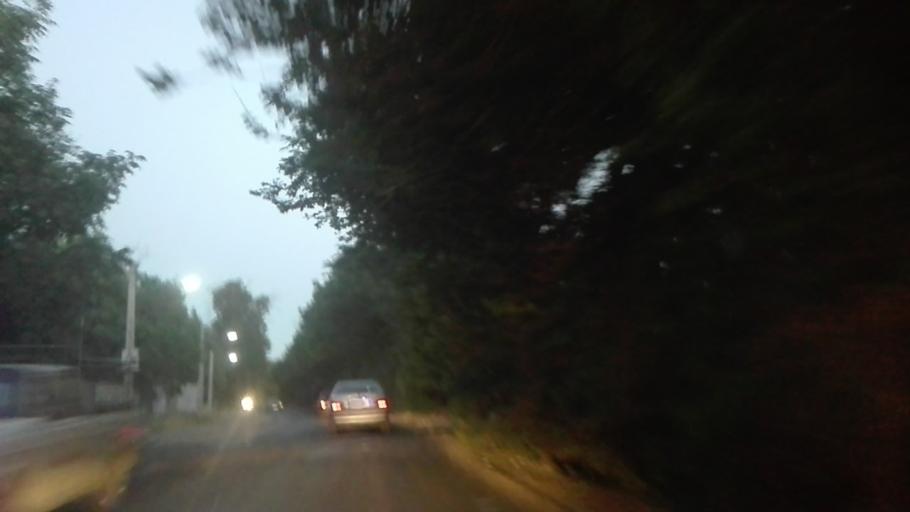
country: IR
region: Tehran
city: Shahriar
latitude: 35.6433
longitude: 51.0558
